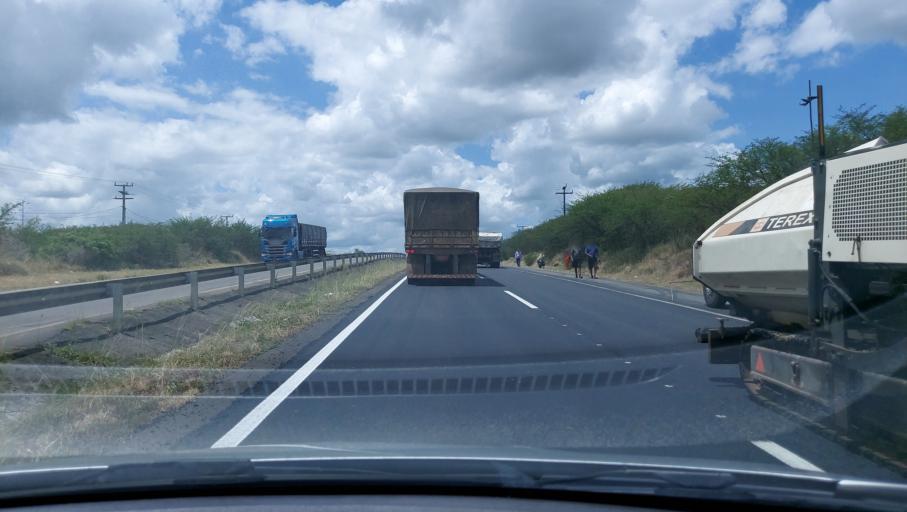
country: BR
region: Bahia
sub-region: Santo Estevao
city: Santo Estevao
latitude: -12.4250
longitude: -39.2054
